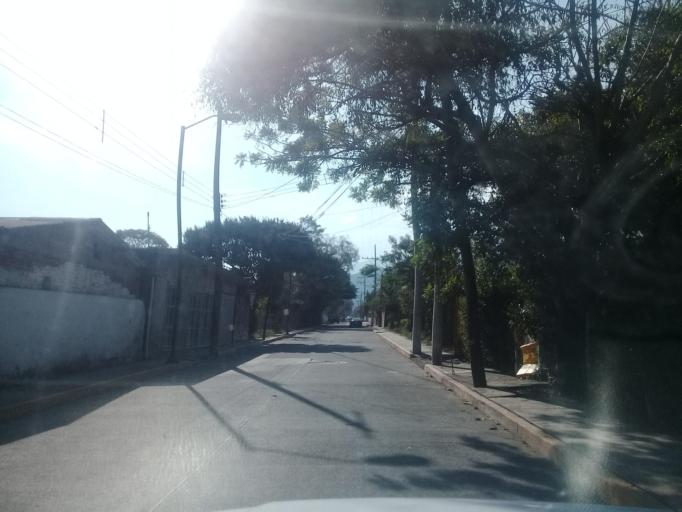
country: MX
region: Veracruz
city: Jalapilla
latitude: 18.8428
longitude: -97.0797
